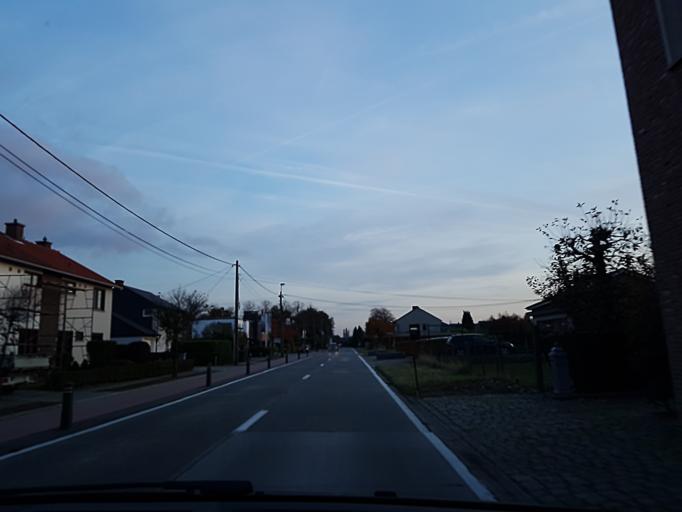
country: BE
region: Flanders
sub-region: Provincie Antwerpen
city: Lier
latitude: 51.1577
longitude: 4.5759
